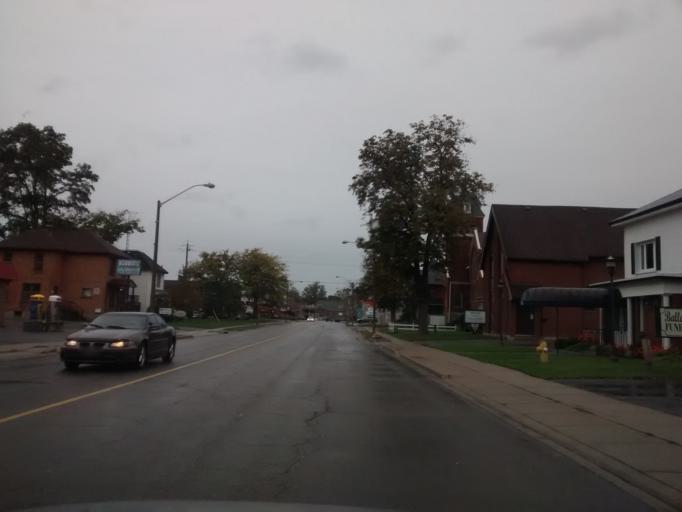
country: CA
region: Ontario
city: Welland
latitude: 42.9035
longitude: -79.6138
